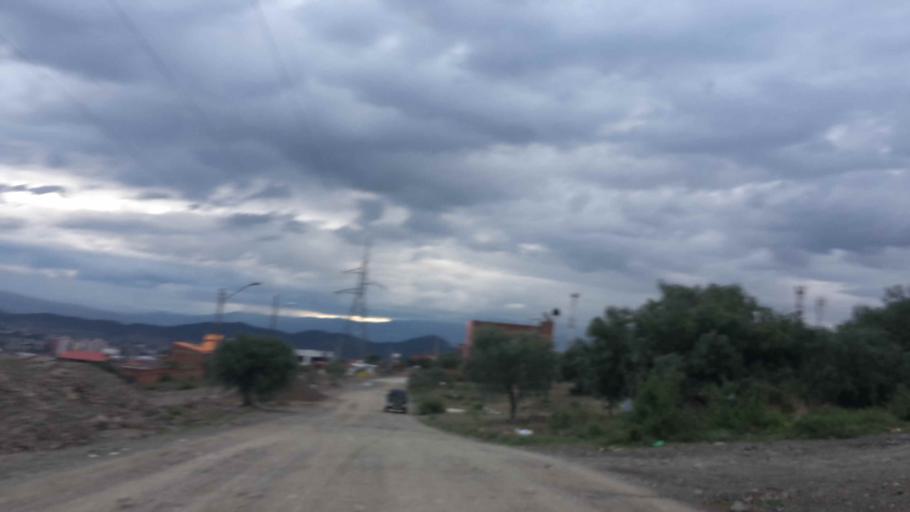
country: BO
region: Cochabamba
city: Cochabamba
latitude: -17.3790
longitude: -66.0696
